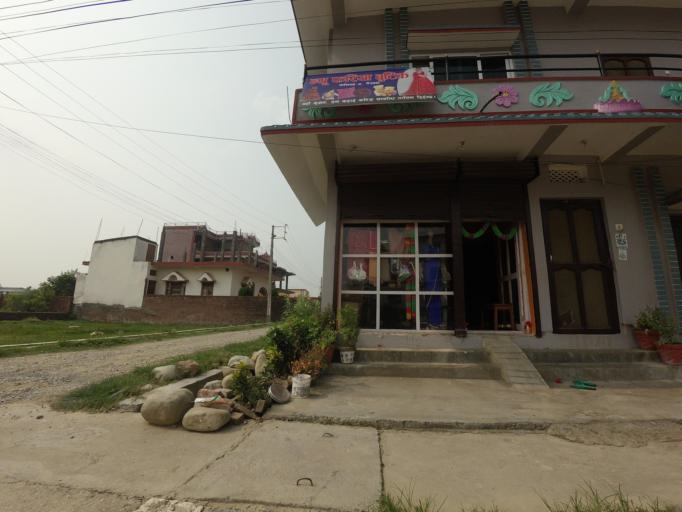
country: NP
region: Western Region
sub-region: Lumbini Zone
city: Bhairahawa
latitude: 27.5261
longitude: 83.4616
